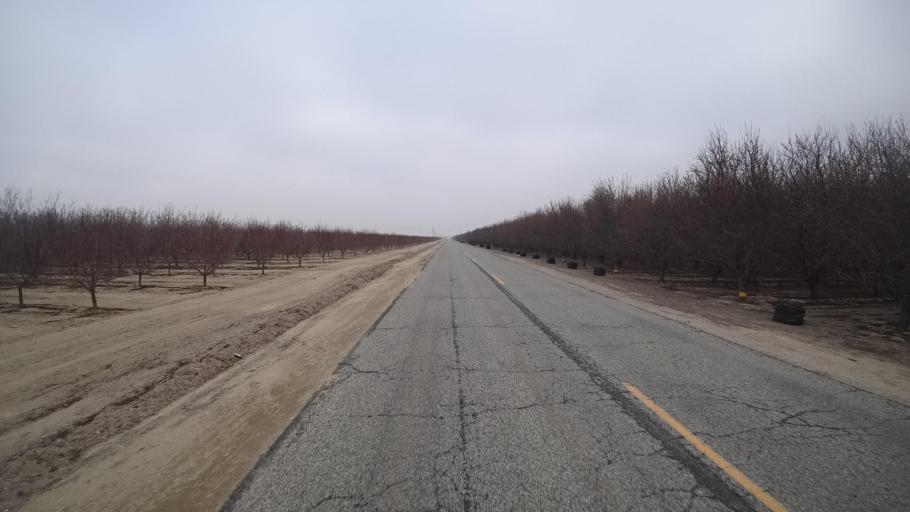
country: US
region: California
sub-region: Kern County
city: Maricopa
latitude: 35.1231
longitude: -119.3541
